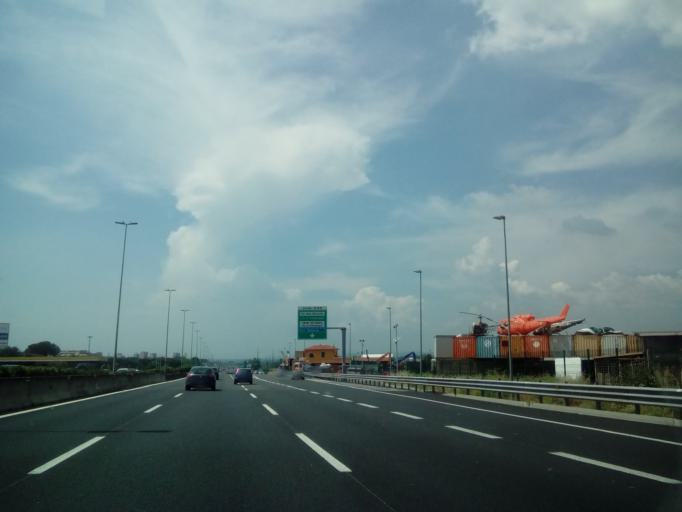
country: IT
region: Latium
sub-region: Citta metropolitana di Roma Capitale
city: Colle Verde
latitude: 41.9730
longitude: 12.5488
